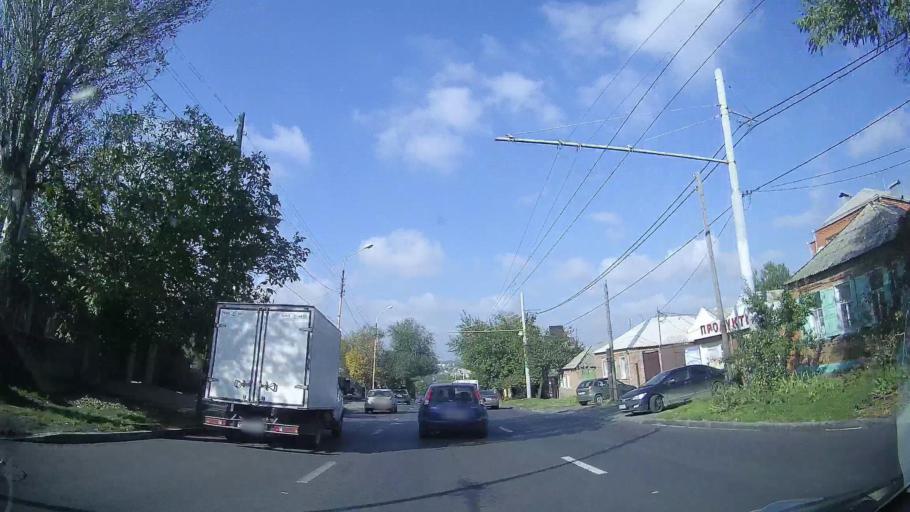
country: RU
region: Rostov
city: Severnyy
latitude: 47.2568
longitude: 39.6968
